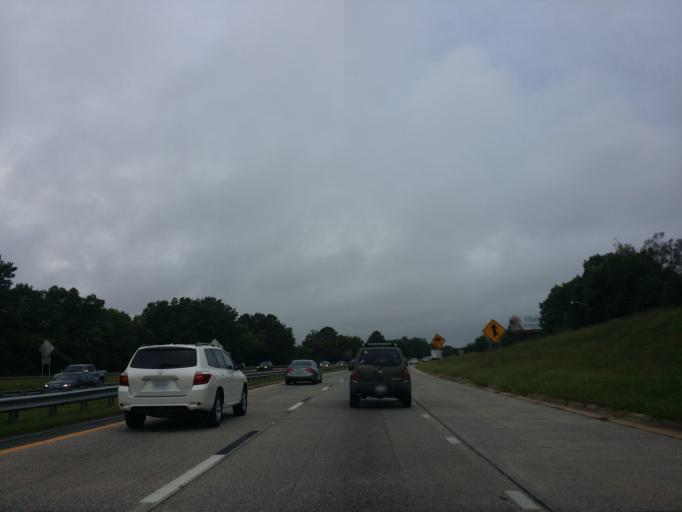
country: US
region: North Carolina
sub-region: Durham County
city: Durham
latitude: 35.9829
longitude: -78.8916
